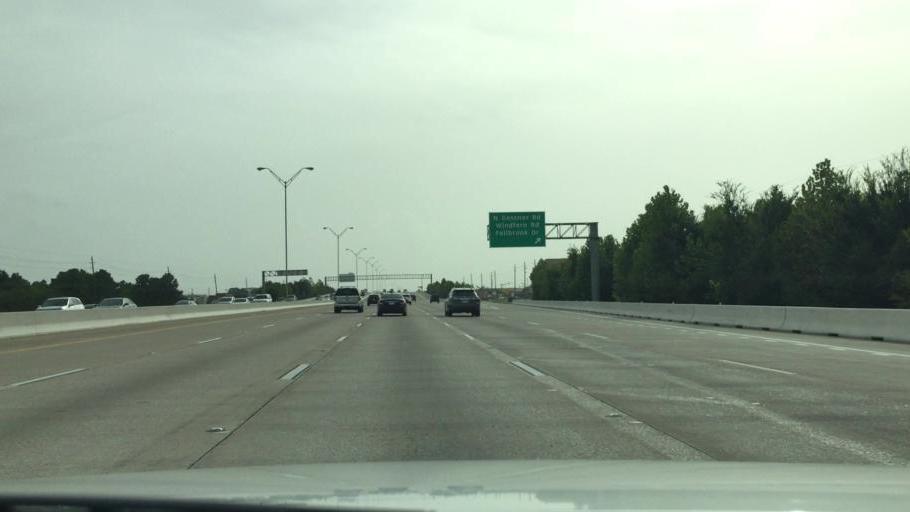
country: US
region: Texas
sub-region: Harris County
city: Hudson
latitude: 29.9321
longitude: -95.5379
